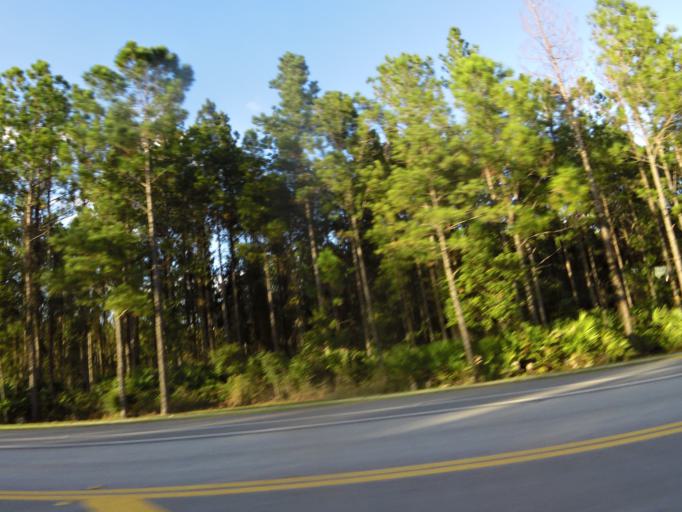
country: US
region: Florida
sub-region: Saint Johns County
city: Fruit Cove
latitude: 30.0581
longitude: -81.6286
